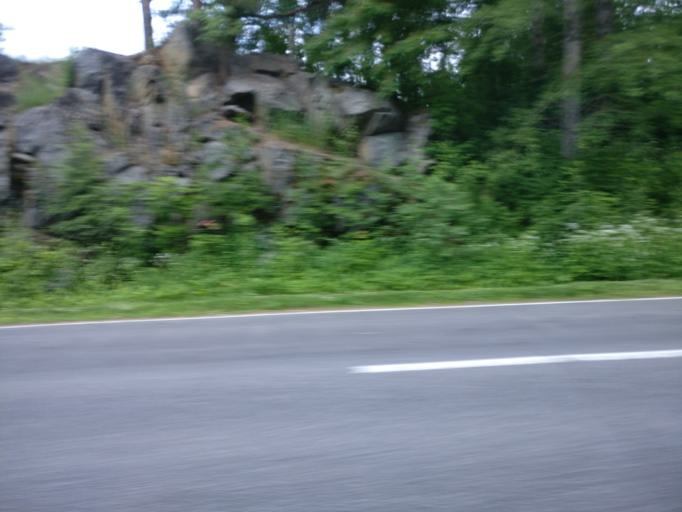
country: FI
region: Southern Savonia
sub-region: Savonlinna
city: Savonlinna
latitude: 61.9139
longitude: 28.9196
